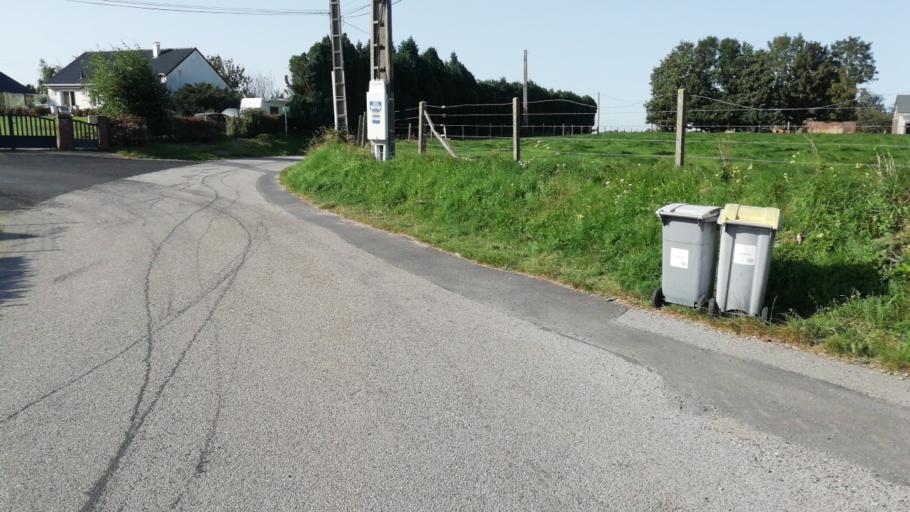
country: FR
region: Haute-Normandie
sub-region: Departement de la Seine-Maritime
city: Etainhus
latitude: 49.5706
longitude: 0.3122
